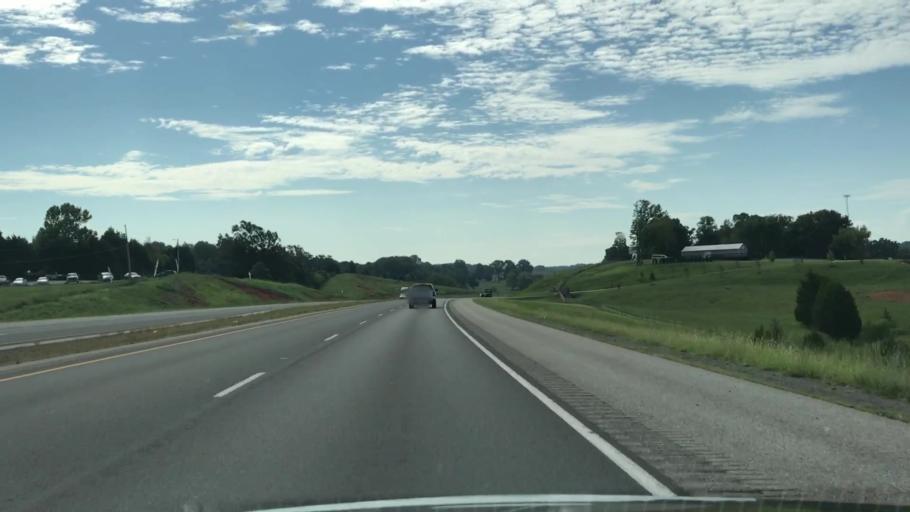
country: US
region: Kentucky
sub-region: Warren County
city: Plano
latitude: 36.8345
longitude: -86.3164
